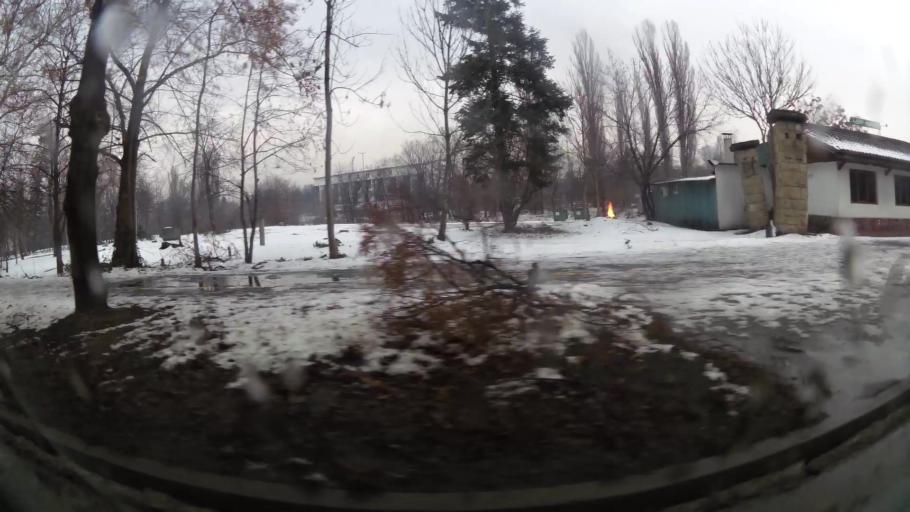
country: BG
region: Sofia-Capital
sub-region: Stolichna Obshtina
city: Sofia
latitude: 42.6749
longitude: 23.2689
